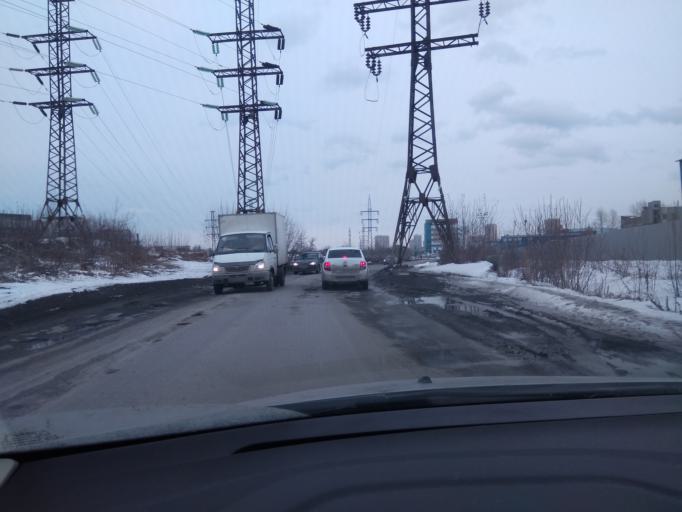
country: RU
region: Sverdlovsk
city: Yekaterinburg
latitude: 56.8760
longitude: 60.6272
